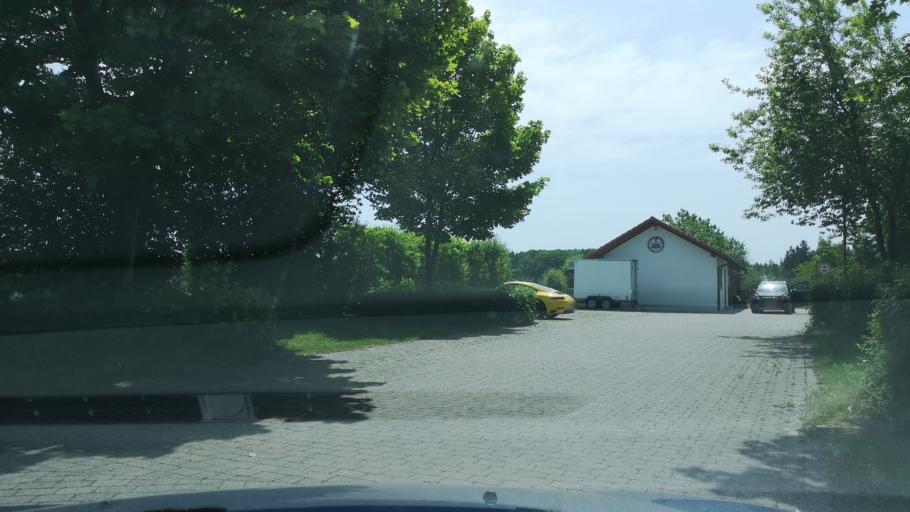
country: DE
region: Bavaria
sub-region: Upper Bavaria
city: Anzing
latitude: 48.1393
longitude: 11.8560
